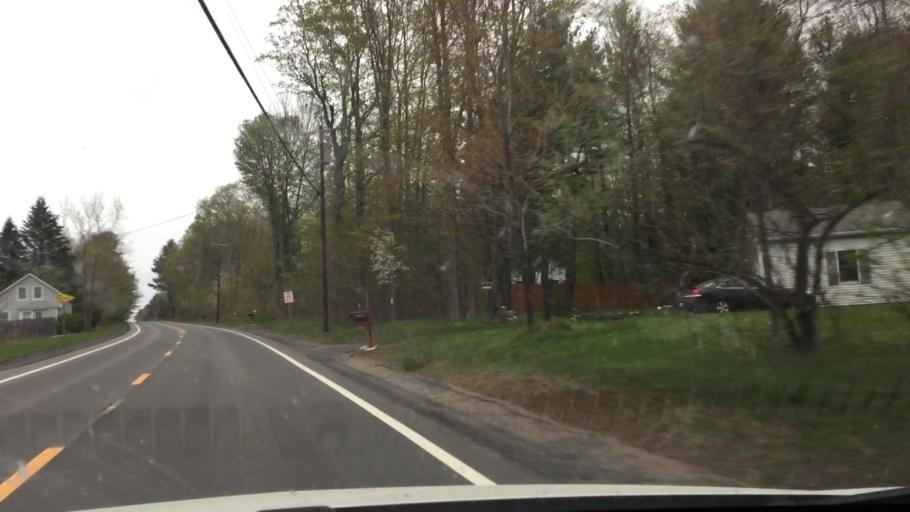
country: US
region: Massachusetts
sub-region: Berkshire County
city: Becket
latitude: 42.2667
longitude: -73.0514
